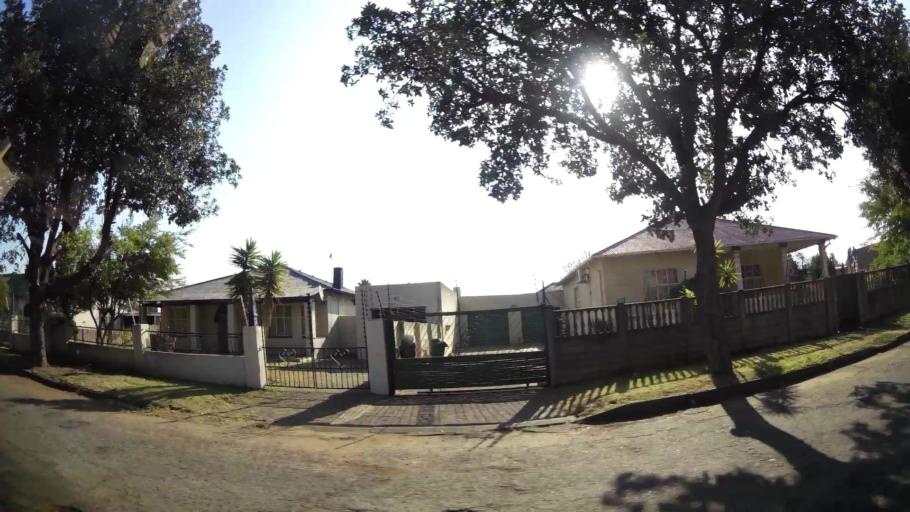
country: ZA
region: Gauteng
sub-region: West Rand District Municipality
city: Randfontein
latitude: -26.1690
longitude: 27.7101
